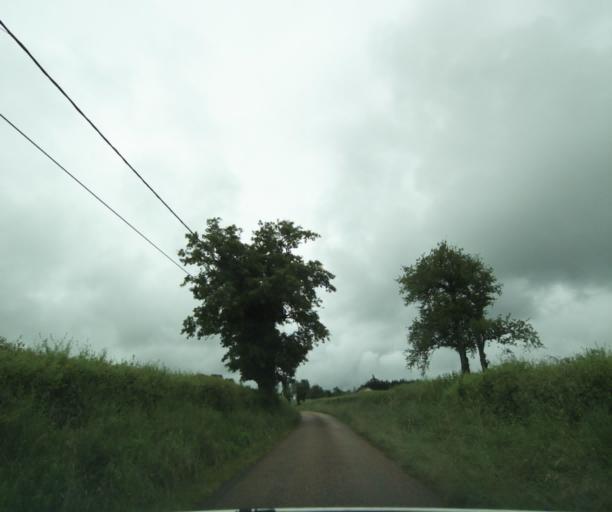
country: FR
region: Bourgogne
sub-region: Departement de Saone-et-Loire
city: Charolles
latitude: 46.4554
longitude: 4.3783
